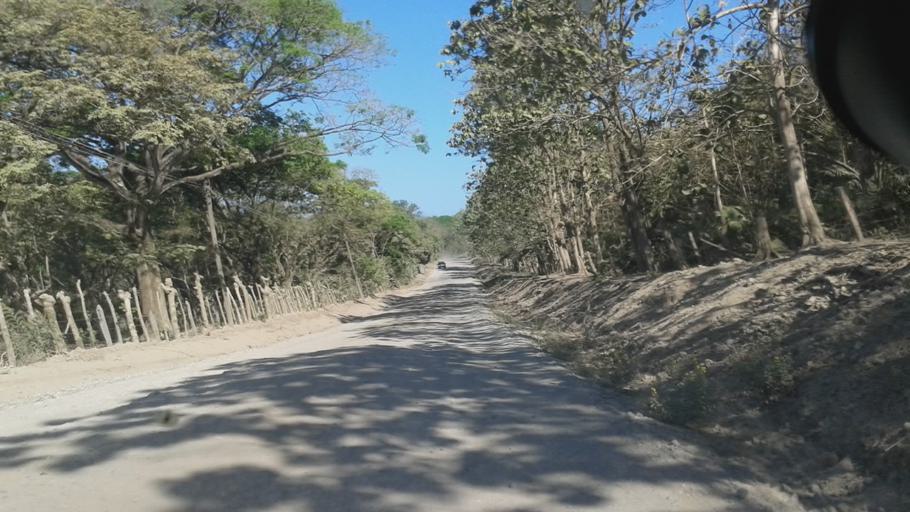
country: CR
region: Guanacaste
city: Samara
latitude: 9.9103
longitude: -85.6020
